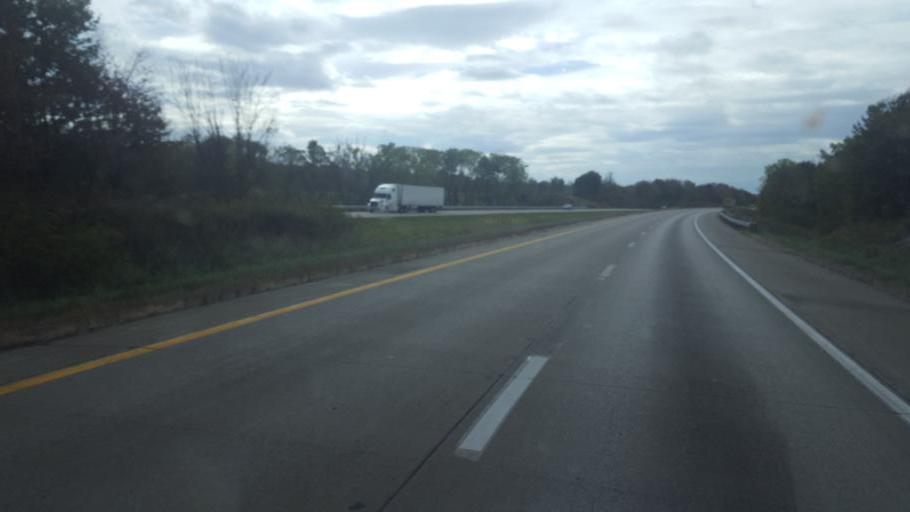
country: US
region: Pennsylvania
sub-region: Mercer County
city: Mercer
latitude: 41.1852
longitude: -80.2833
